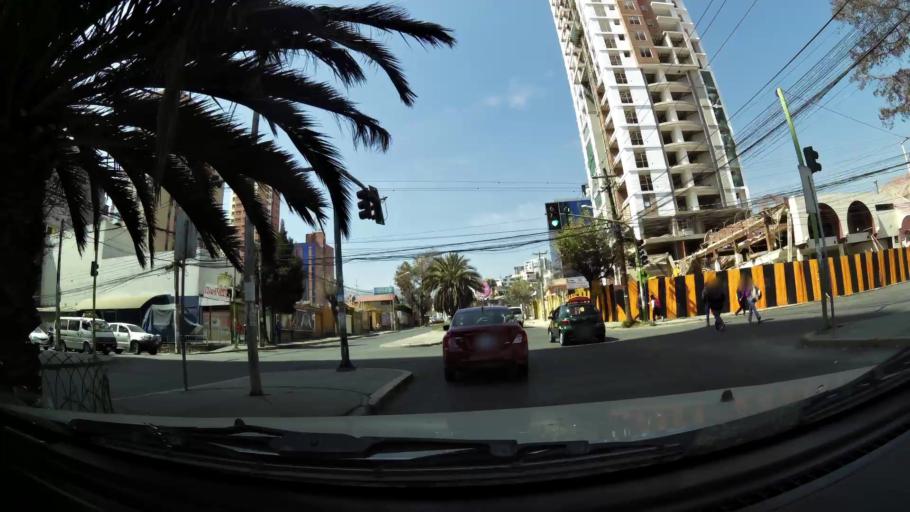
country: BO
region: La Paz
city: La Paz
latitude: -16.5391
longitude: -68.0769
